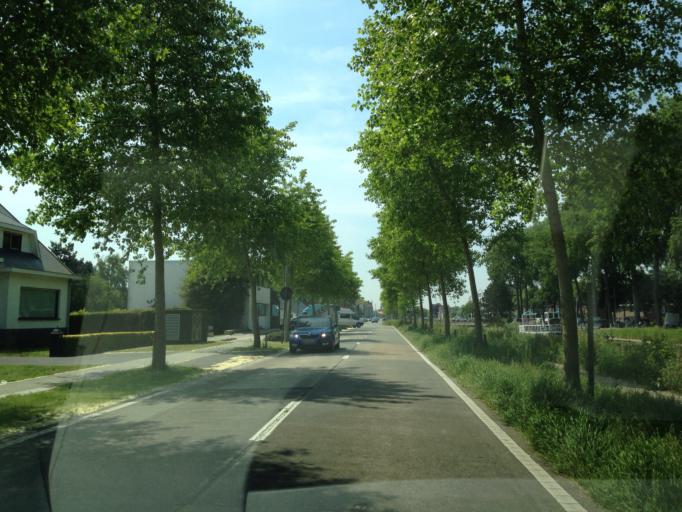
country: BE
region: Flanders
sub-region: Provincie West-Vlaanderen
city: Sint-Kruis
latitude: 51.2256
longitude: 3.2426
